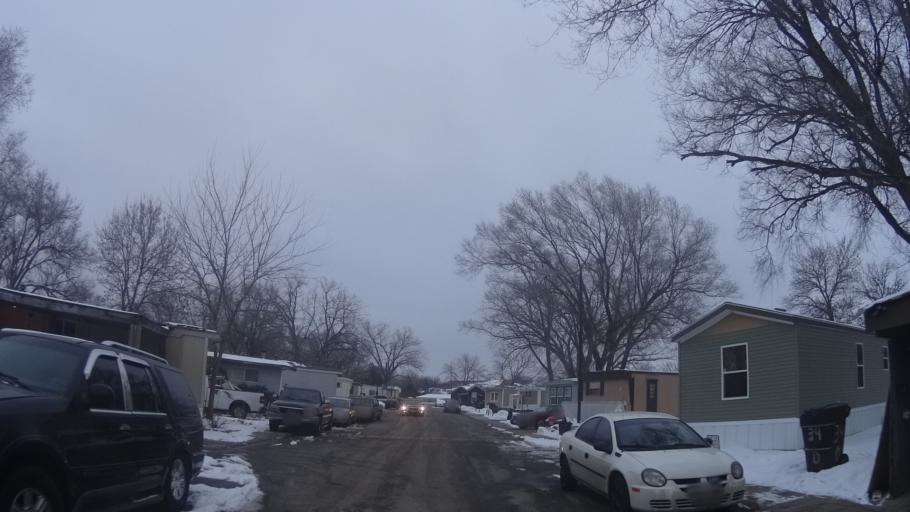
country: US
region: Nebraska
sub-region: Sarpy County
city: Offutt Air Force Base
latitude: 41.1384
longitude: -95.9221
